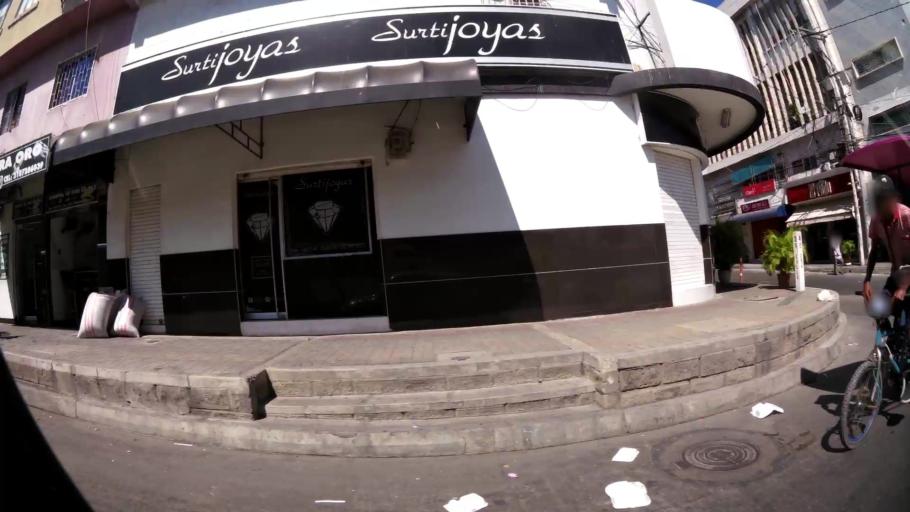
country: CO
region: Atlantico
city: Barranquilla
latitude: 10.9802
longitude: -74.7819
